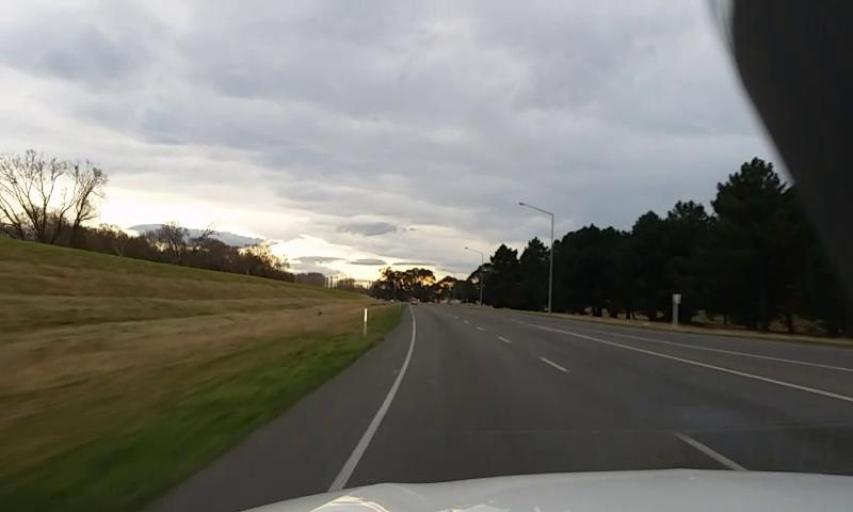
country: NZ
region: Canterbury
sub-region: Waimakariri District
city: Kaiapoi
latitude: -43.4277
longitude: 172.6467
